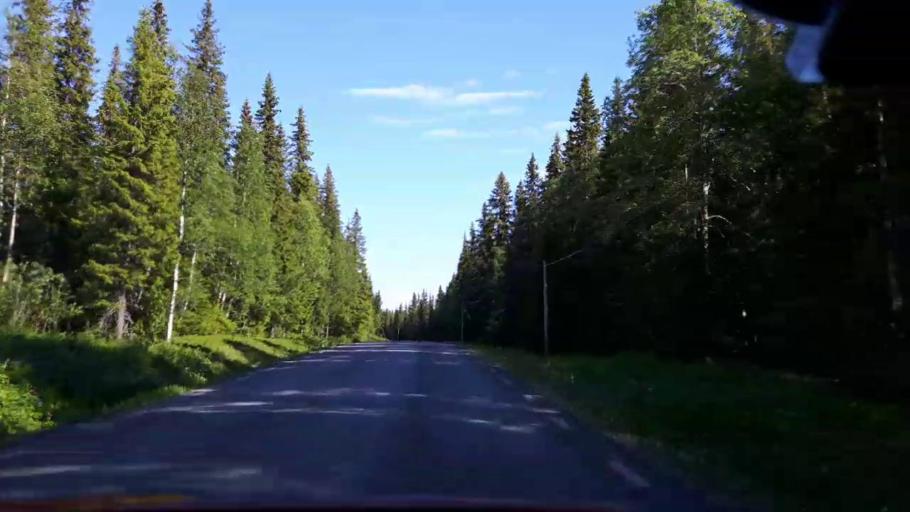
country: SE
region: Jaemtland
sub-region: Krokoms Kommun
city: Valla
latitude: 63.7216
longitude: 14.1249
